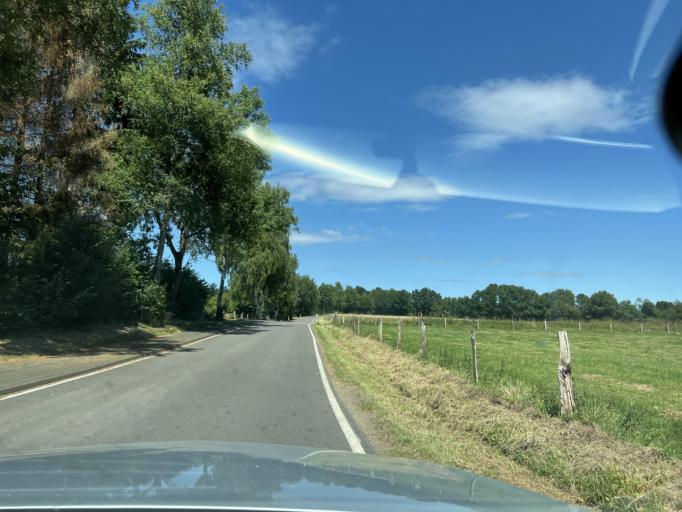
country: DE
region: North Rhine-Westphalia
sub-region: Regierungsbezirk Arnsberg
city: Wenden
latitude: 50.9474
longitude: 7.8923
